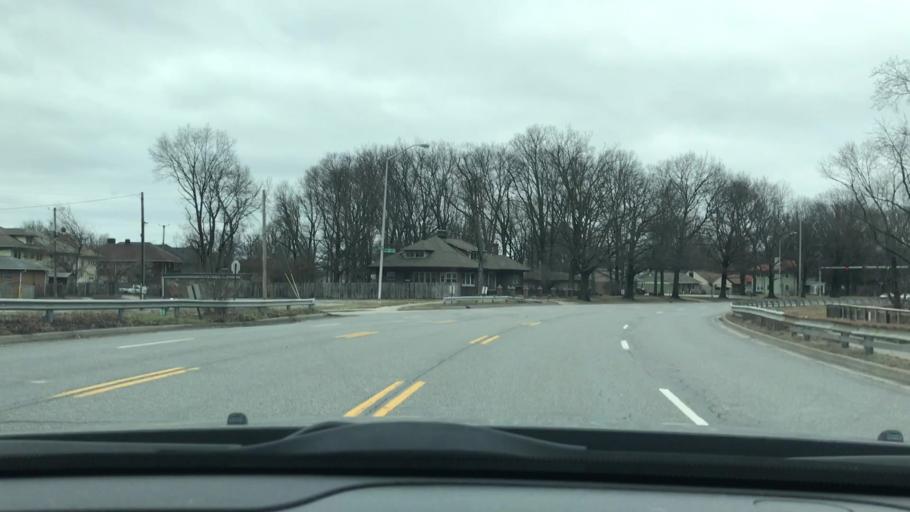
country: US
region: Indiana
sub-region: Marion County
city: Indianapolis
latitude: 39.8137
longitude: -86.1438
